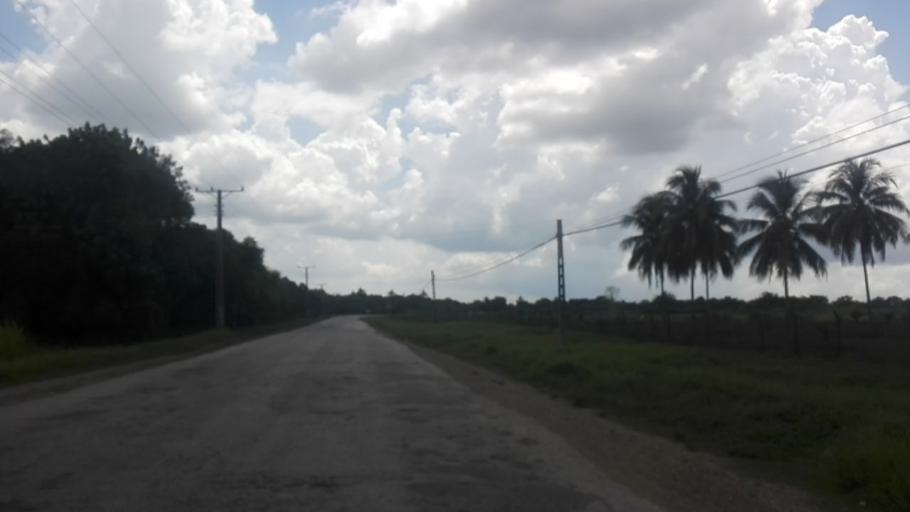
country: CU
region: Granma
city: Bartolome Maso
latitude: 20.1423
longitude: -76.9642
